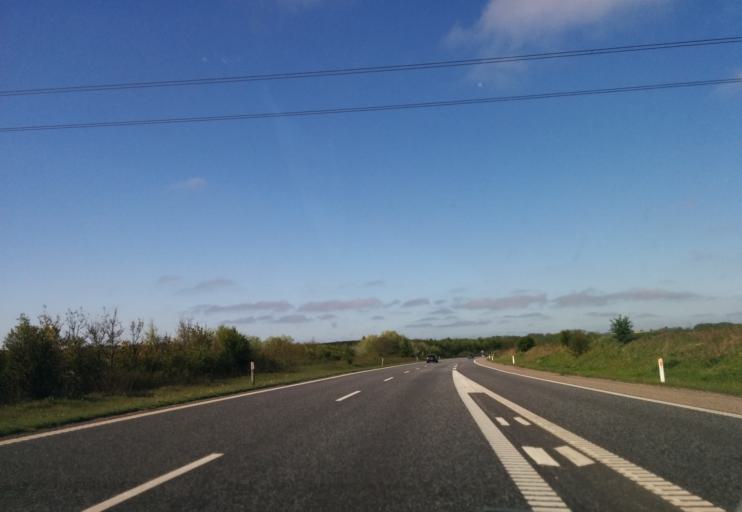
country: DK
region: Central Jutland
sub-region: Skanderborg Kommune
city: Horning
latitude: 56.1055
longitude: 10.0468
